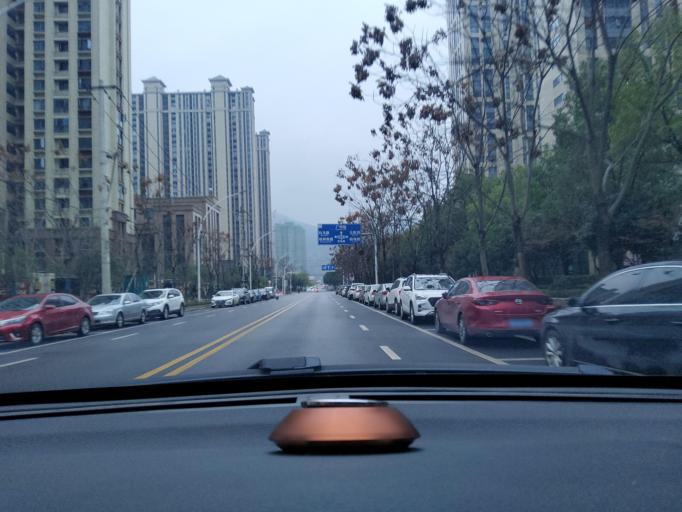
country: CN
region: Hubei
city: Tuanchengshan
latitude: 30.1971
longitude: 115.0094
